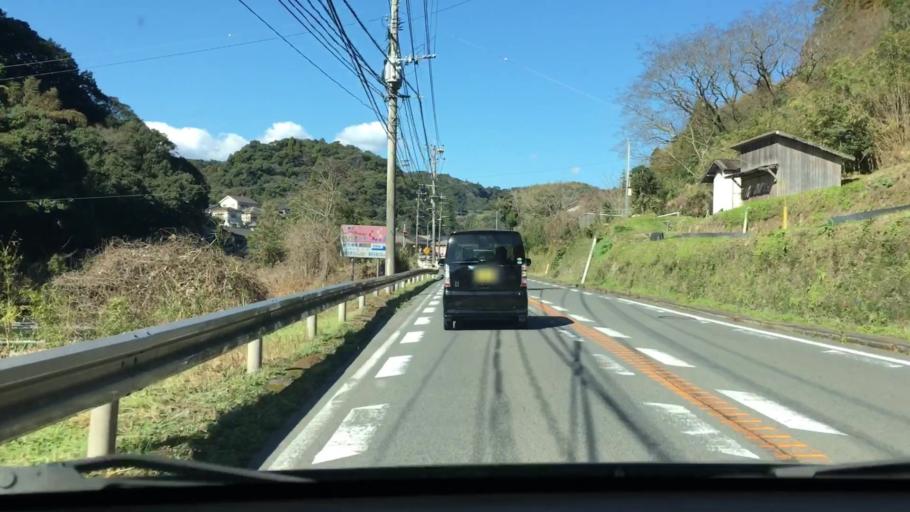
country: JP
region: Kagoshima
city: Kagoshima-shi
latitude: 31.6487
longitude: 130.5137
